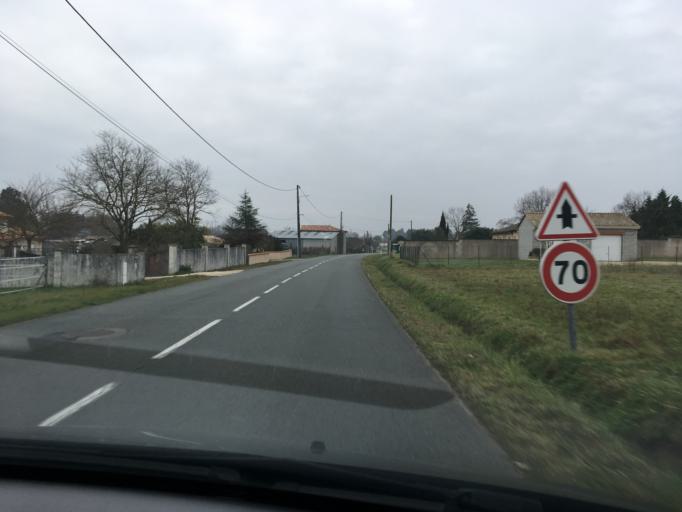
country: FR
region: Aquitaine
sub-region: Departement de la Gironde
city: Saint-Ciers-sur-Gironde
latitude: 45.2823
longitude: -0.6008
